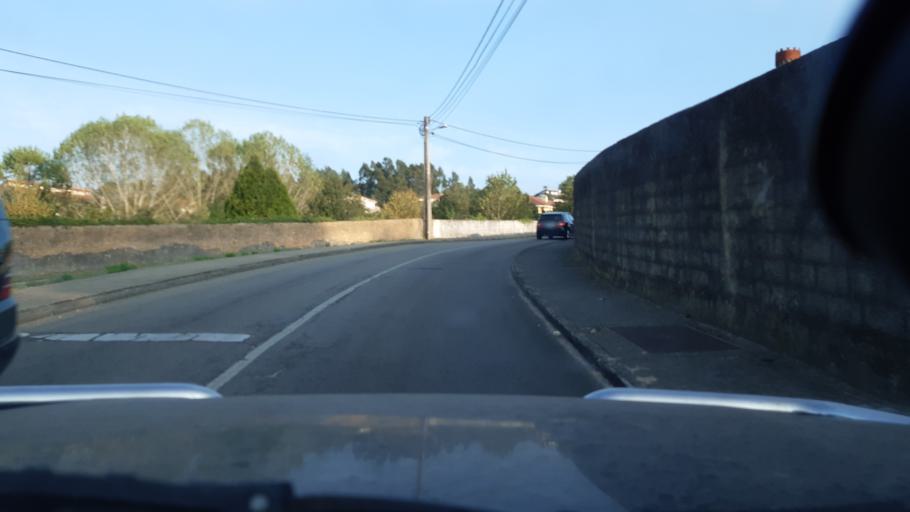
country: PT
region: Aveiro
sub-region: Agueda
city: Agueda
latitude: 40.5591
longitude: -8.4354
